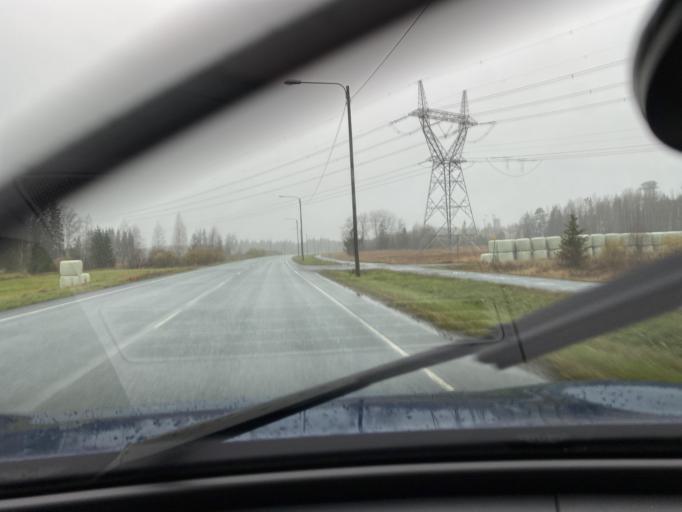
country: FI
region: Haeme
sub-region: Forssa
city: Forssa
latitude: 60.8009
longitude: 23.5703
